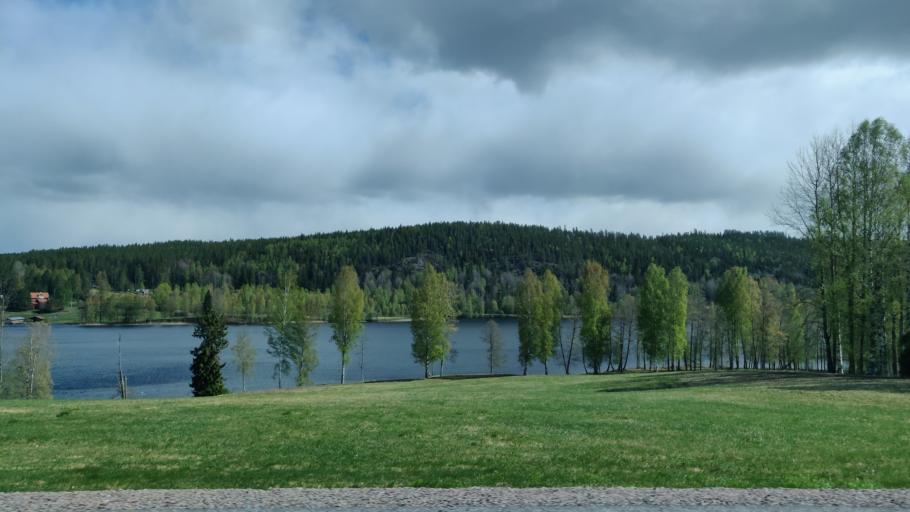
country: SE
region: Vaermland
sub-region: Hagfors Kommun
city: Hagfors
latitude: 59.9131
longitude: 13.6715
